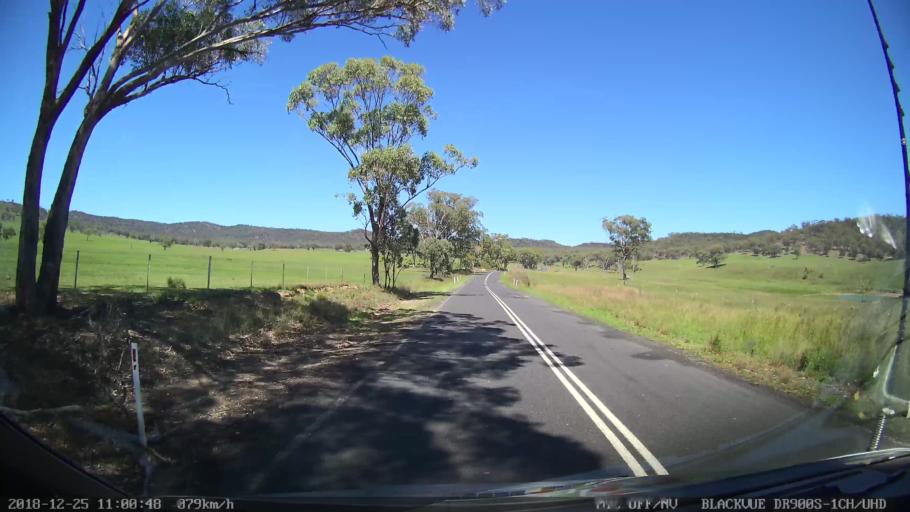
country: AU
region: New South Wales
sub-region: Upper Hunter Shire
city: Merriwa
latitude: -32.4027
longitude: 150.2103
